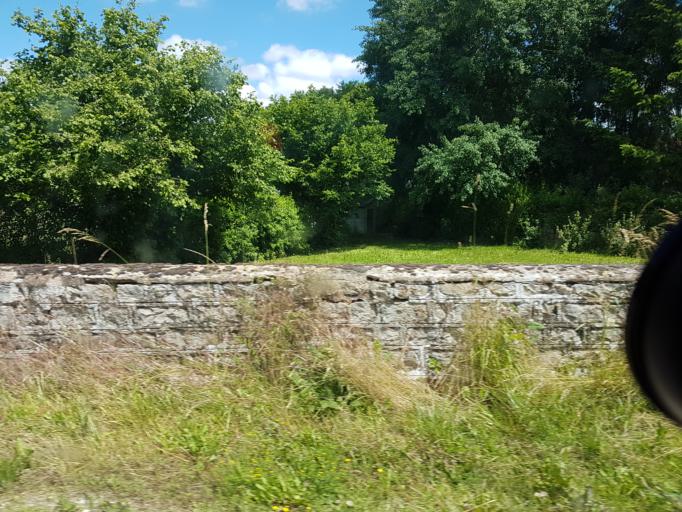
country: FR
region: Bourgogne
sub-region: Departement de Saone-et-Loire
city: Curgy
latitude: 47.0467
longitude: 4.3758
